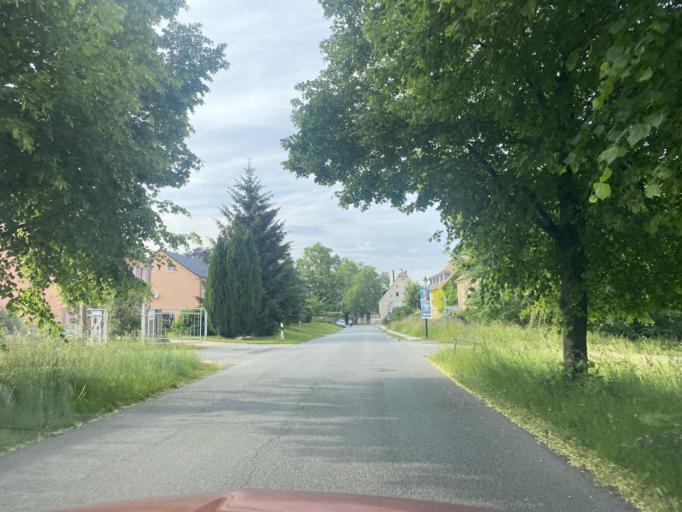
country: DE
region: Saxony
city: Herrnhut
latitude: 51.0247
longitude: 14.7598
